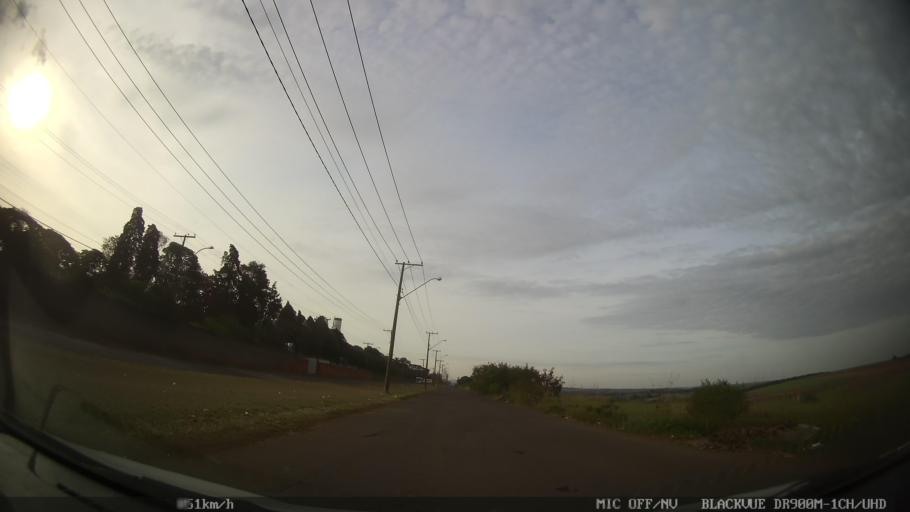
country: BR
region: Sao Paulo
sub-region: Piracicaba
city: Piracicaba
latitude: -22.7302
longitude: -47.5870
